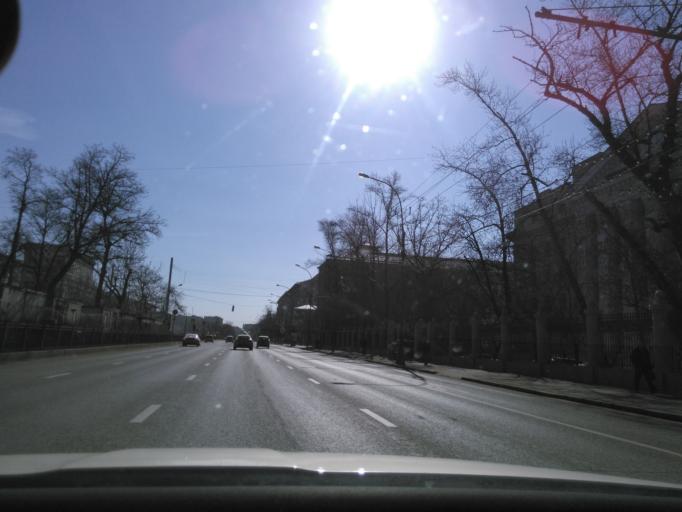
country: RU
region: Moskovskaya
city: Dorogomilovo
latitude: 55.7828
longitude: 37.5709
